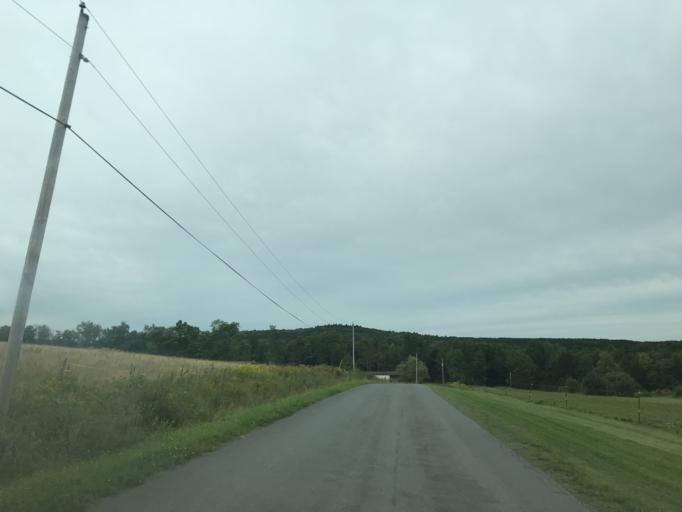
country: US
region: New York
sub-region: Otsego County
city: Worcester
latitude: 42.5850
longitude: -74.6751
